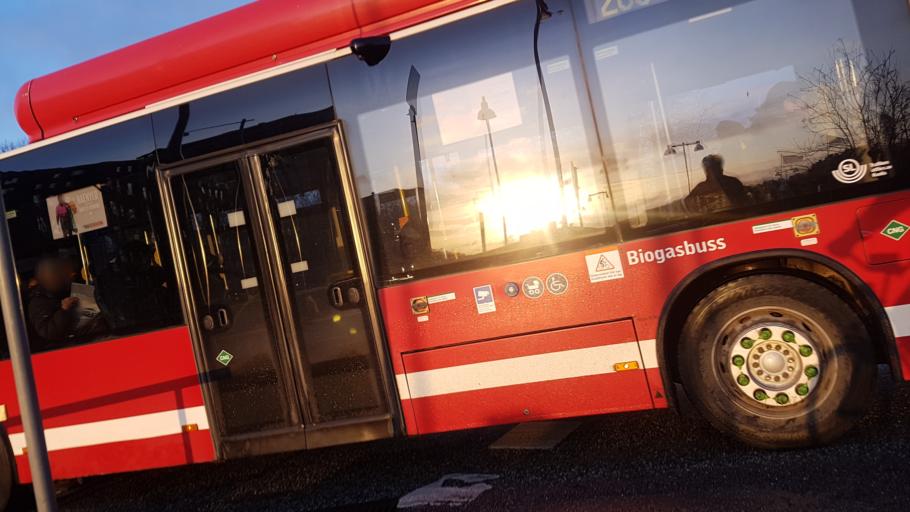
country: SE
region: Stockholm
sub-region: Lidingo
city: Lidingoe
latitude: 59.3503
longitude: 18.1442
